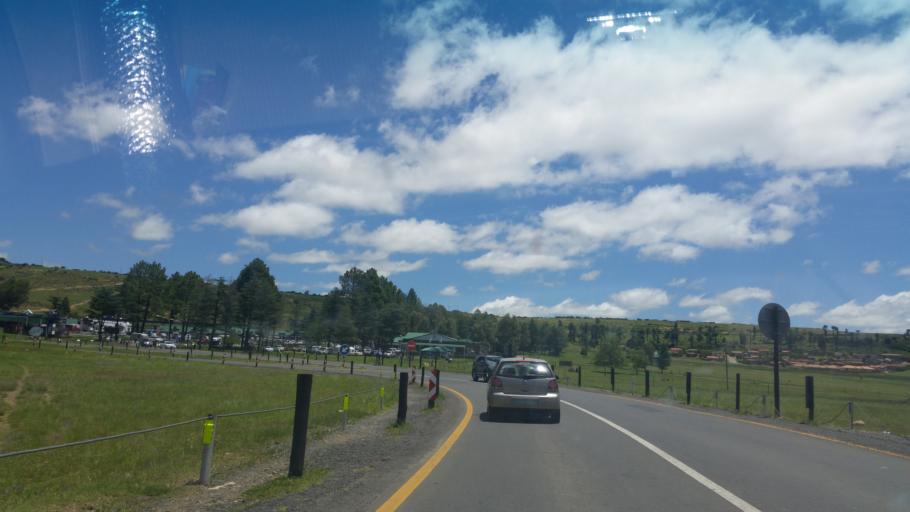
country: ZA
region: Orange Free State
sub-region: Thabo Mofutsanyana District Municipality
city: Harrismith
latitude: -28.2575
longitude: 29.1175
